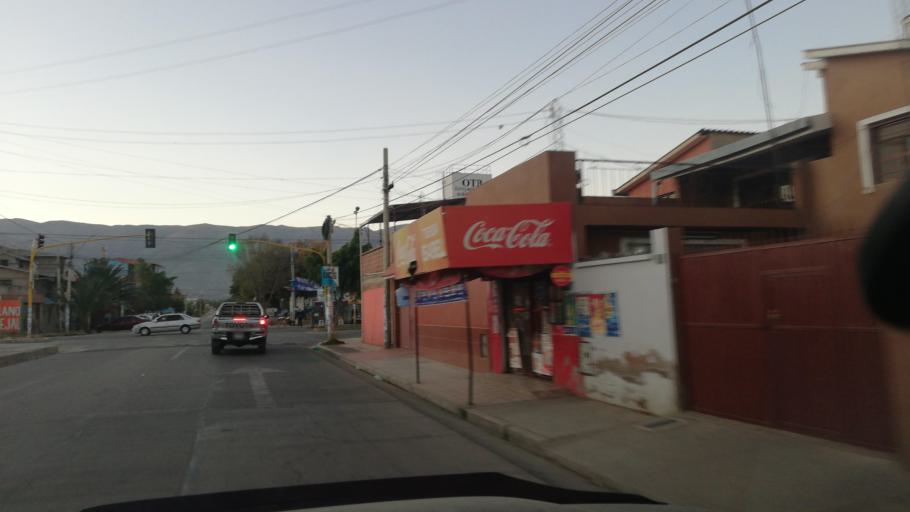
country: BO
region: Cochabamba
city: Cochabamba
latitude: -17.3884
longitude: -66.2191
